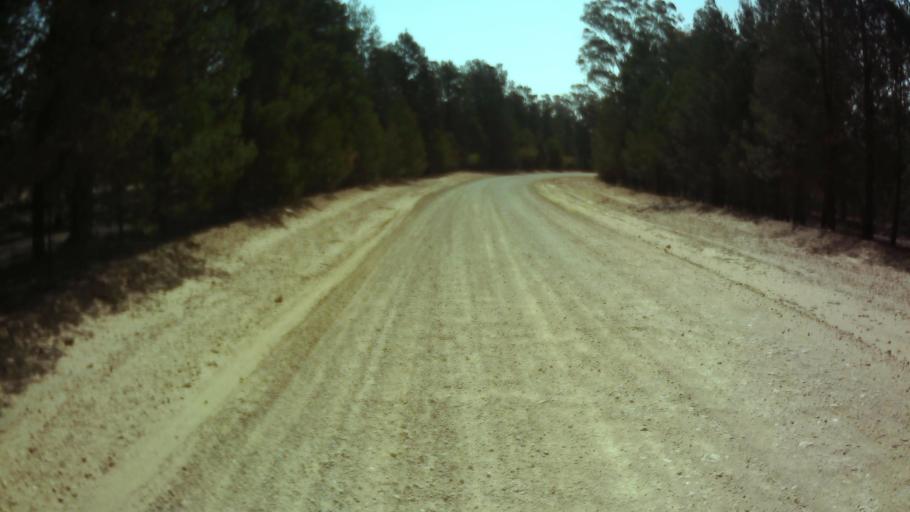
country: AU
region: New South Wales
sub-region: Weddin
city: Grenfell
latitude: -33.9183
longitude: 147.9247
